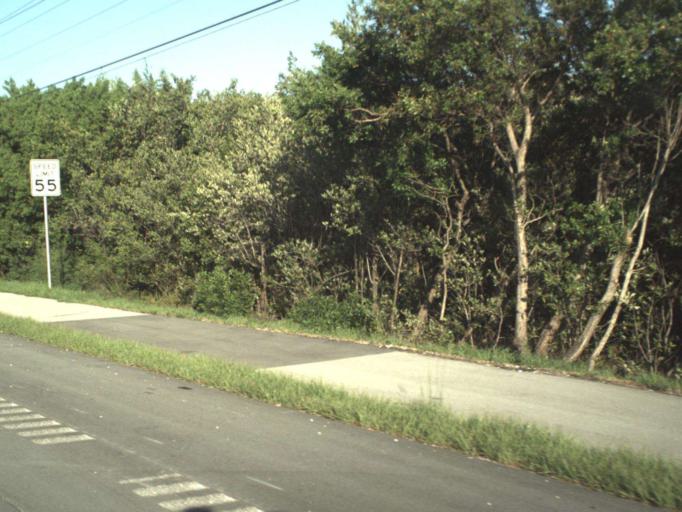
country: US
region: Florida
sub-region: Monroe County
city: Islamorada
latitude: 24.8376
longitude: -80.7982
